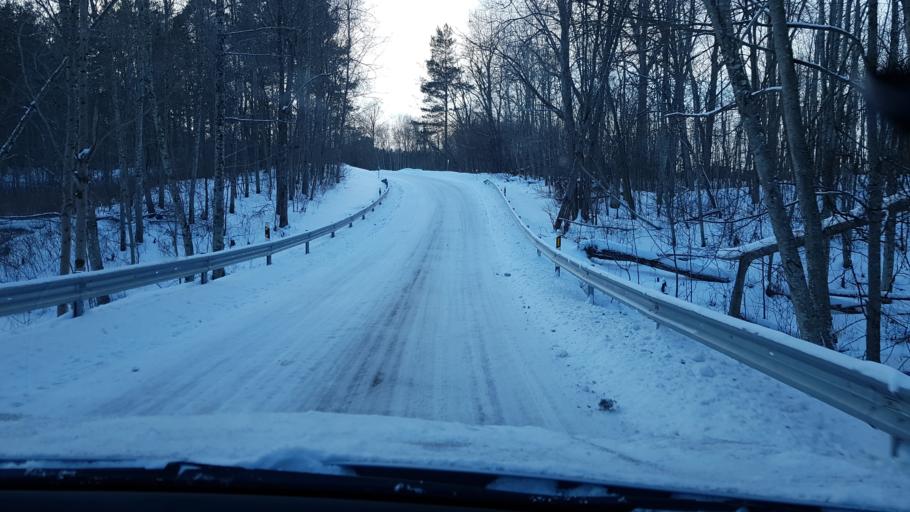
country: EE
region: Harju
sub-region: Nissi vald
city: Turba
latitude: 59.2219
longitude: 24.1435
